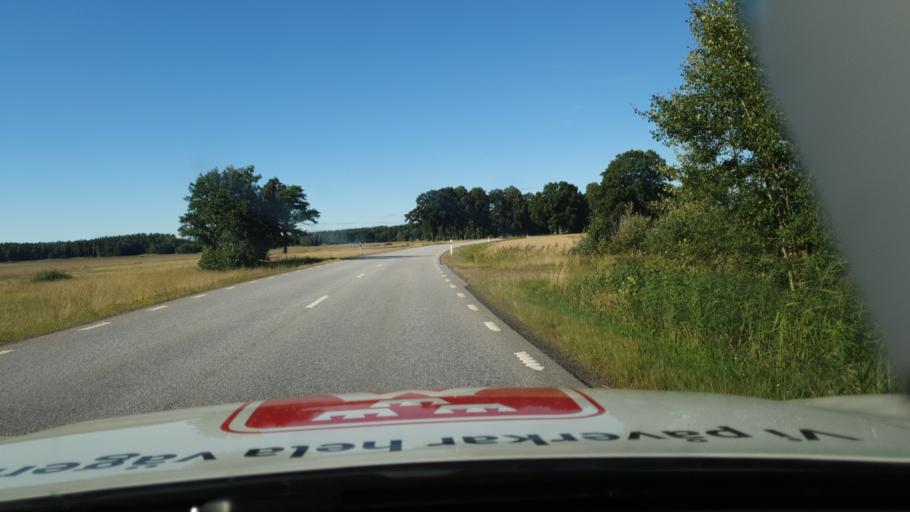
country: SE
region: Vaestra Goetaland
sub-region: Toreboda Kommun
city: Toereboda
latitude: 58.6144
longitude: 14.0109
